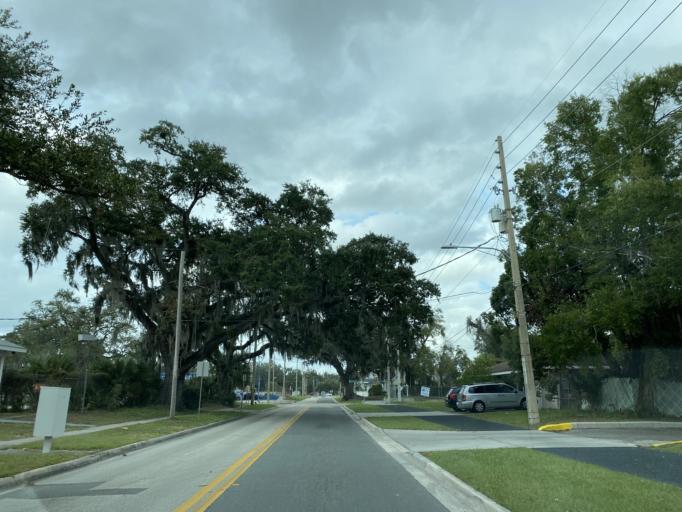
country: US
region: Florida
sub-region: Orange County
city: Orlando
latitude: 28.5505
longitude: -81.3933
